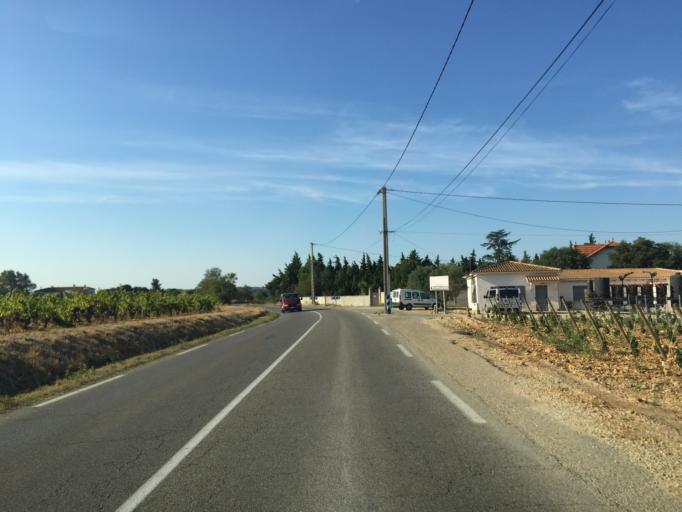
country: FR
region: Provence-Alpes-Cote d'Azur
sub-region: Departement du Vaucluse
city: Sorgues
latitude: 44.0346
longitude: 4.8575
